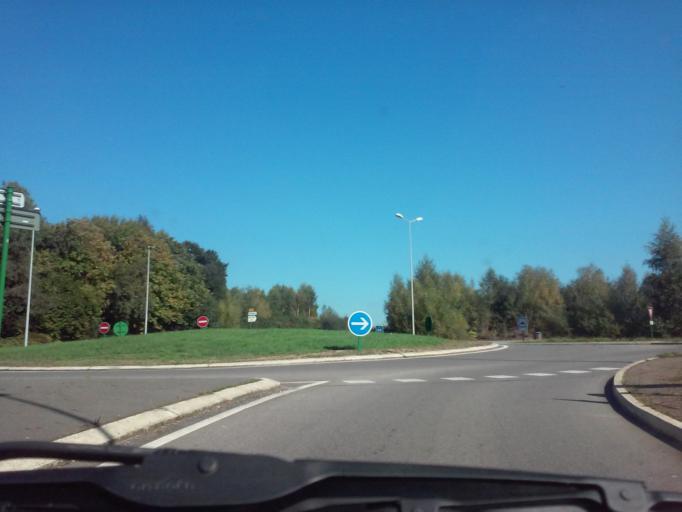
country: FR
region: Brittany
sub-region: Departement d'Ille-et-Vilaine
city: Chevaigne
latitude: 48.2092
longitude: -1.6248
